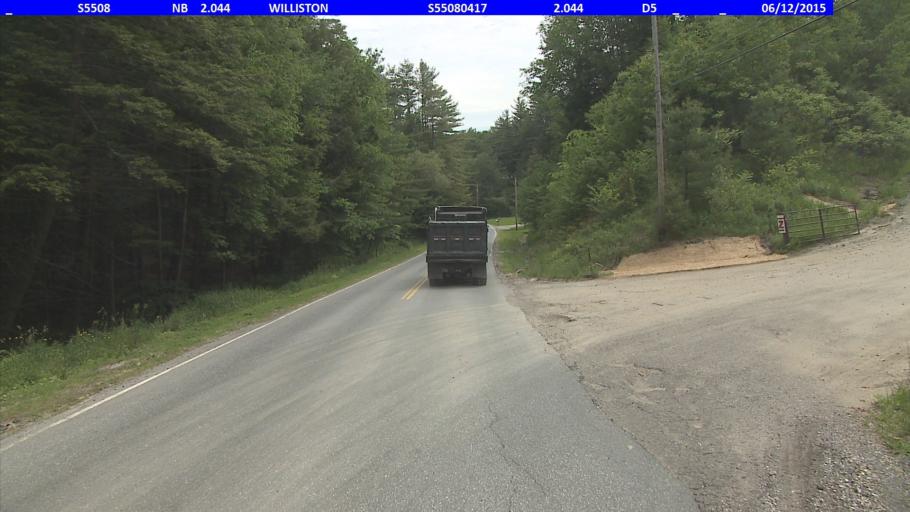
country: US
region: Vermont
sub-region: Chittenden County
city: Williston
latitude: 44.4618
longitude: -73.0523
